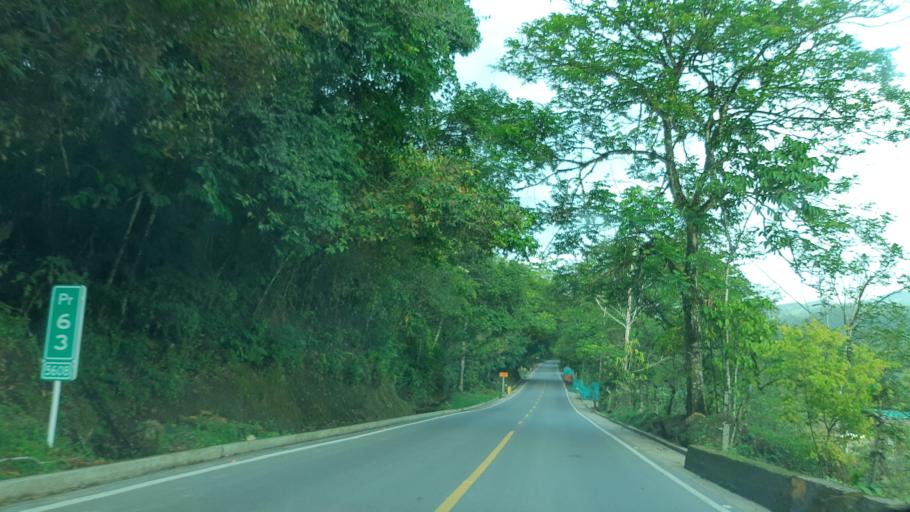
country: CO
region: Boyaca
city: San Luis de Gaceno
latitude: 4.8176
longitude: -73.1878
